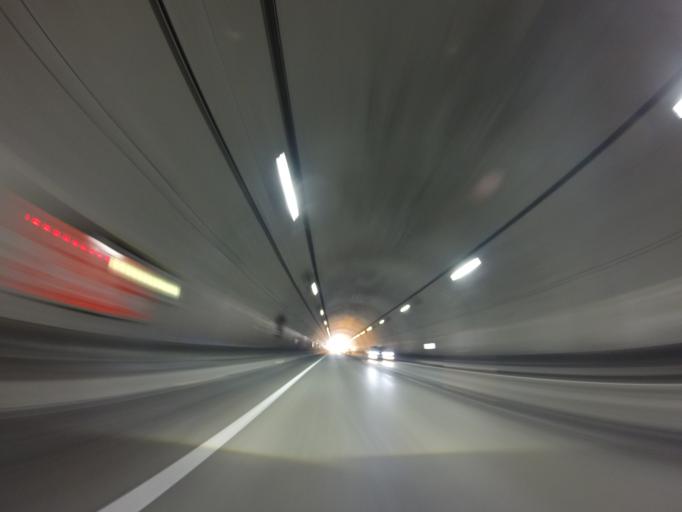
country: JP
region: Shizuoka
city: Ito
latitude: 34.9712
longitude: 138.9372
